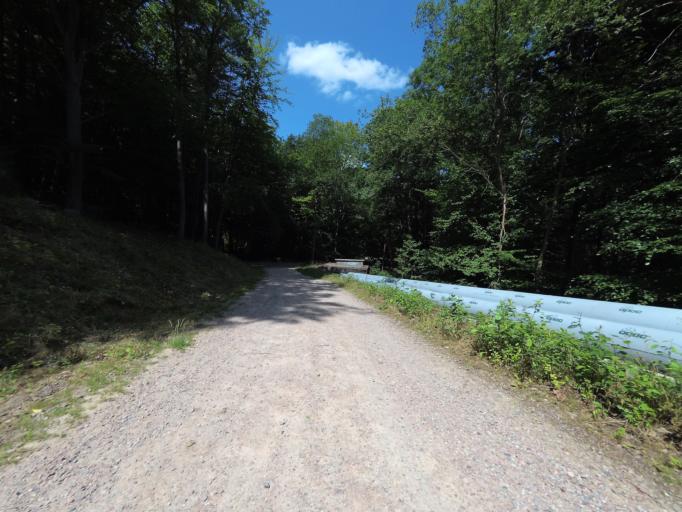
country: PL
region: Pomeranian Voivodeship
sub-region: Gdynia
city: Wielki Kack
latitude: 54.4879
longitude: 18.5024
